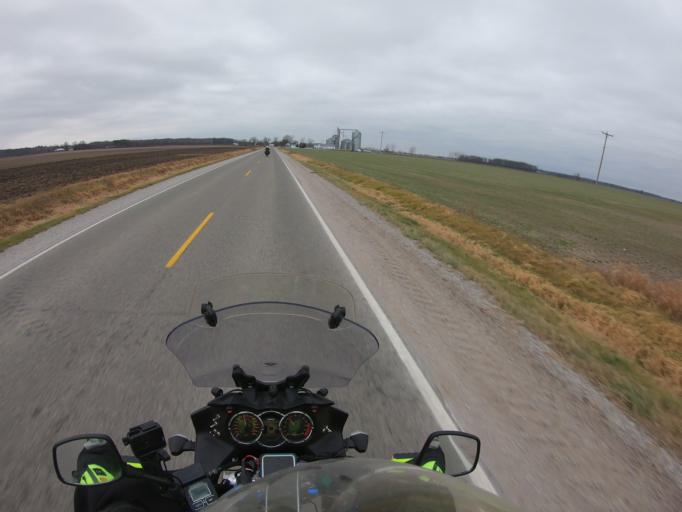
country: US
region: Michigan
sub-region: Saginaw County
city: Chesaning
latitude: 43.2557
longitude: -84.0582
